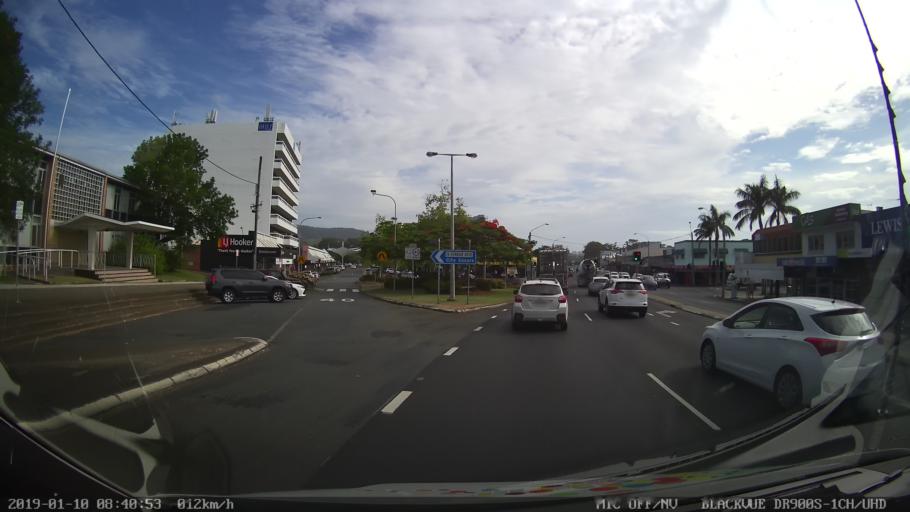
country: AU
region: New South Wales
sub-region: Coffs Harbour
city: Coffs Harbour
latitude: -30.2976
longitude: 153.1127
